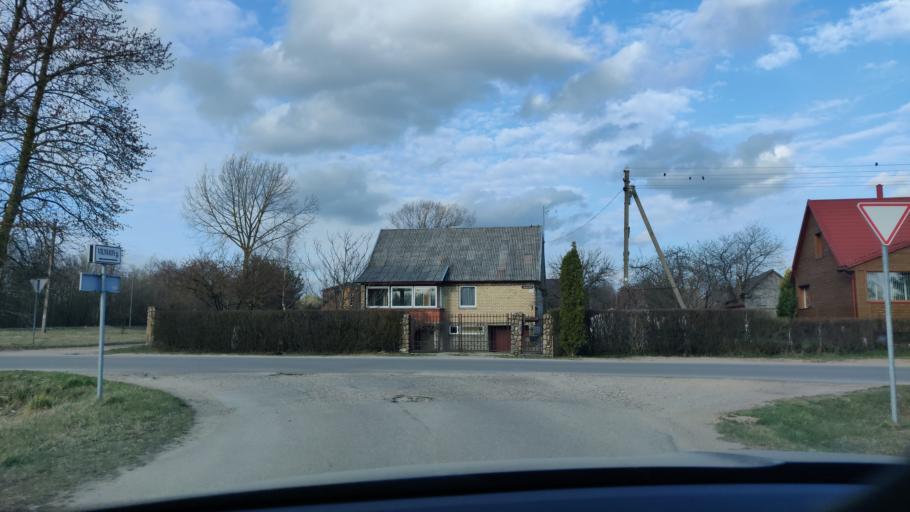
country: LT
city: Trakai
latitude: 54.6092
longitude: 24.9743
